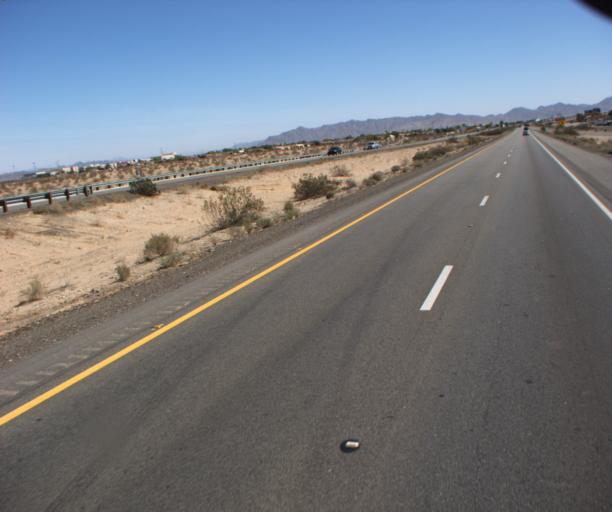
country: US
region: Arizona
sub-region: Yuma County
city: Fortuna Foothills
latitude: 32.6776
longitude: -114.5201
